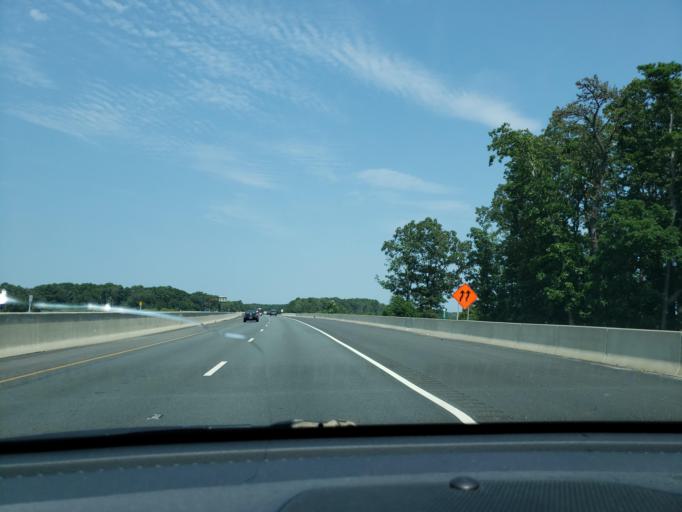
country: US
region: New Jersey
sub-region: Atlantic County
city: Somers Point
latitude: 39.3332
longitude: -74.6081
